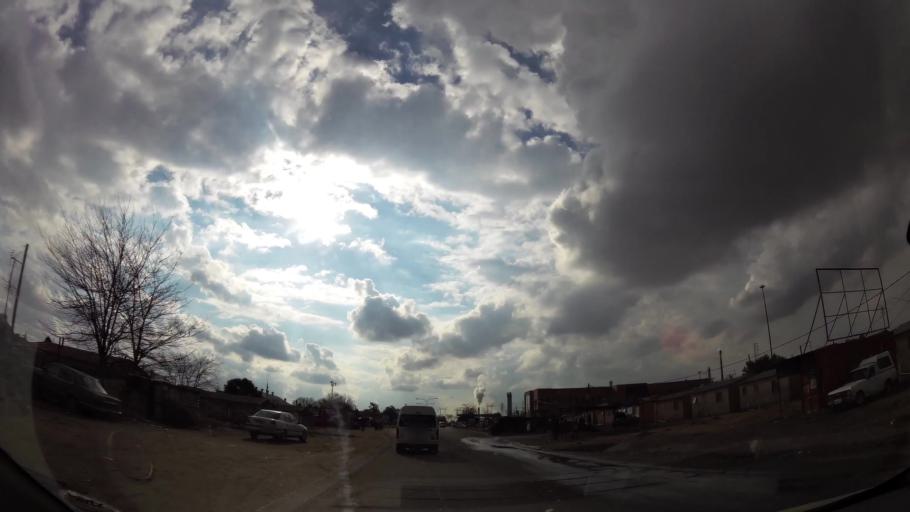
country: ZA
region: Orange Free State
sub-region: Fezile Dabi District Municipality
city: Sasolburg
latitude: -26.8382
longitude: 27.8442
